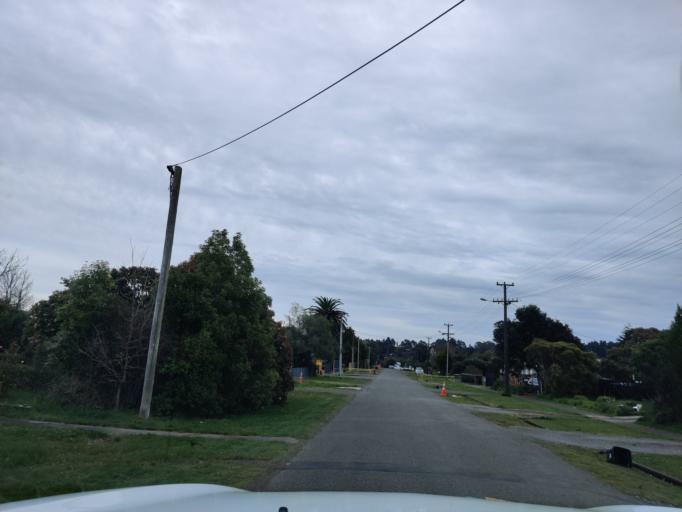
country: NZ
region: Manawatu-Wanganui
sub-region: Palmerston North City
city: Palmerston North
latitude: -40.2856
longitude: 175.7551
